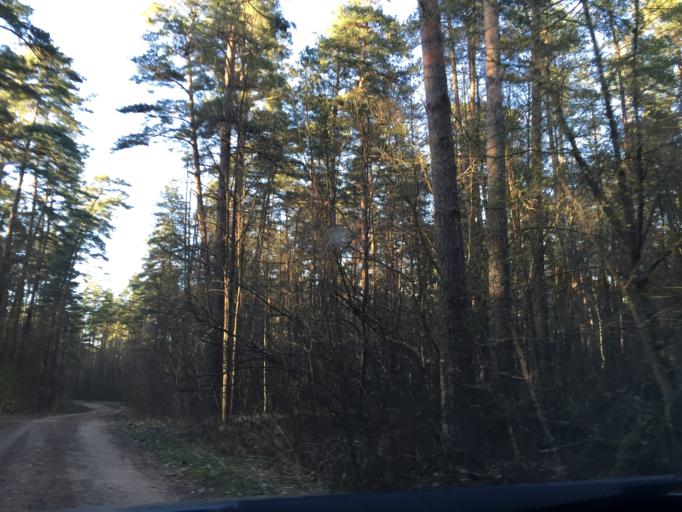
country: LV
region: Kekava
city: Kekava
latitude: 56.8576
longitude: 24.2319
